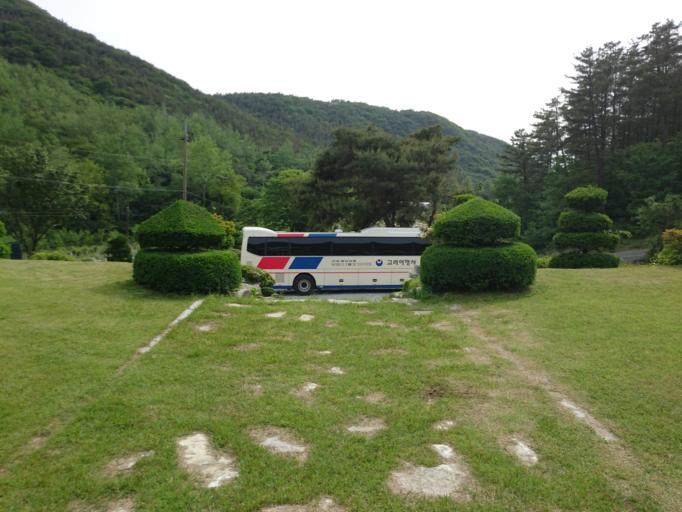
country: KR
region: Jeollabuk-do
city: Wanju
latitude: 35.9055
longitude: 127.2090
